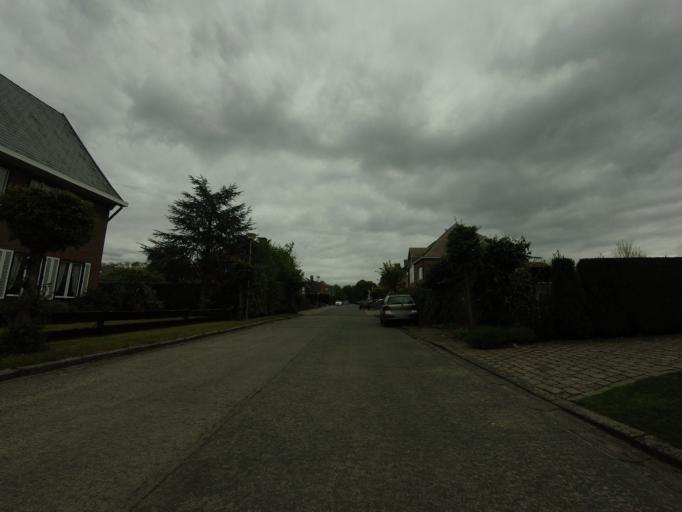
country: BE
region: Flanders
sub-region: Provincie Antwerpen
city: Mechelen
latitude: 51.0470
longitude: 4.4876
